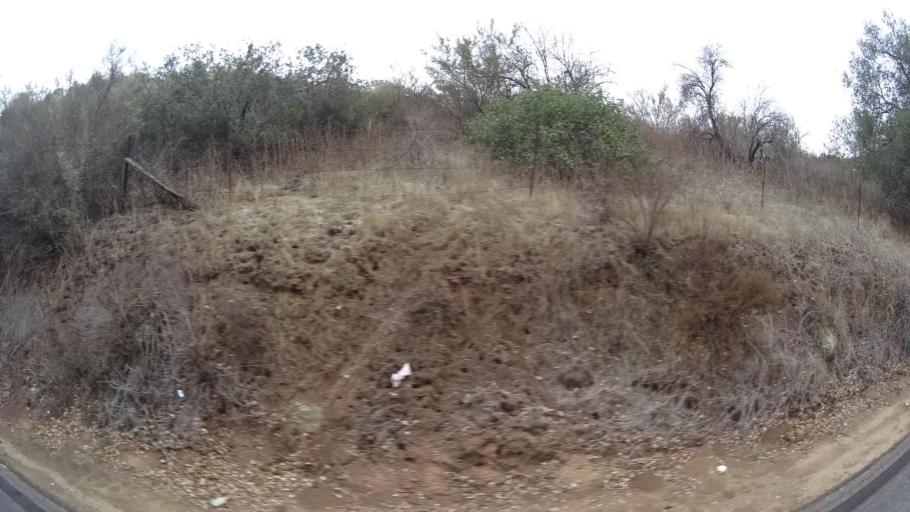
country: US
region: California
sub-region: San Diego County
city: Ramona
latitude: 33.0695
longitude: -116.8905
